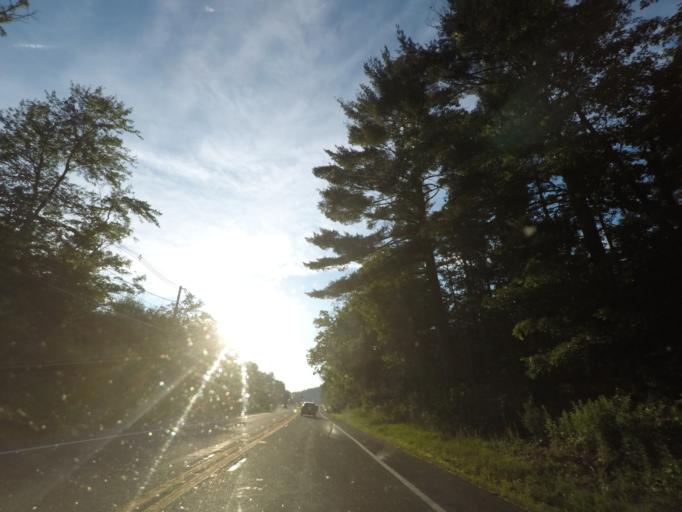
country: US
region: Massachusetts
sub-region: Hampden County
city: Brimfield
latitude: 42.1146
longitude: -72.2307
